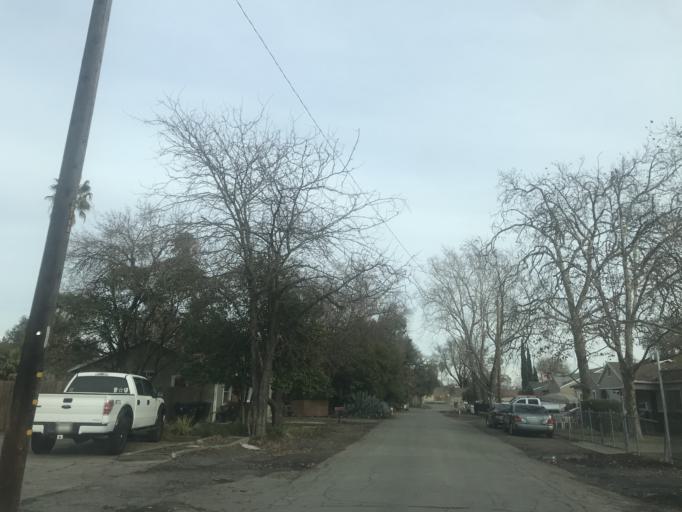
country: US
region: California
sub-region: Sacramento County
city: Parkway
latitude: 38.5300
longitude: -121.4725
